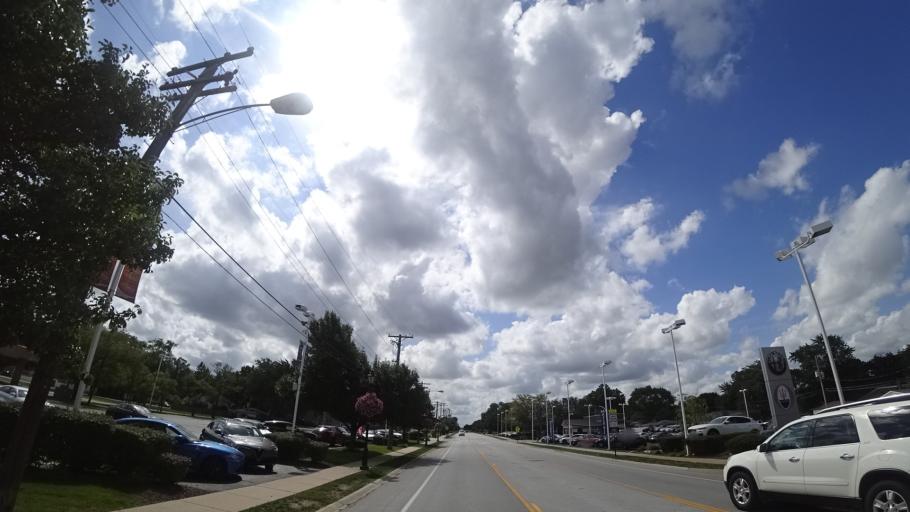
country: US
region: Illinois
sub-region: Cook County
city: Tinley Park
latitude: 41.5721
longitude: -87.7842
